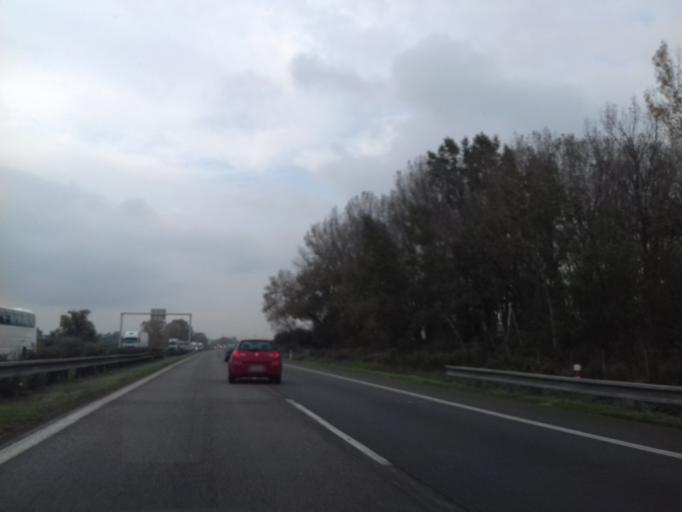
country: SK
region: Bratislavsky
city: Stupava
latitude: 48.2225
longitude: 17.0279
